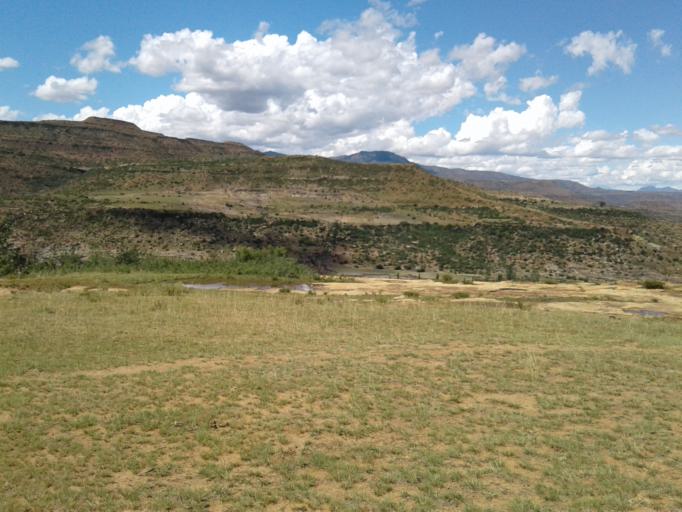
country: LS
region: Quthing
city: Quthing
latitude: -30.3724
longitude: 27.5527
